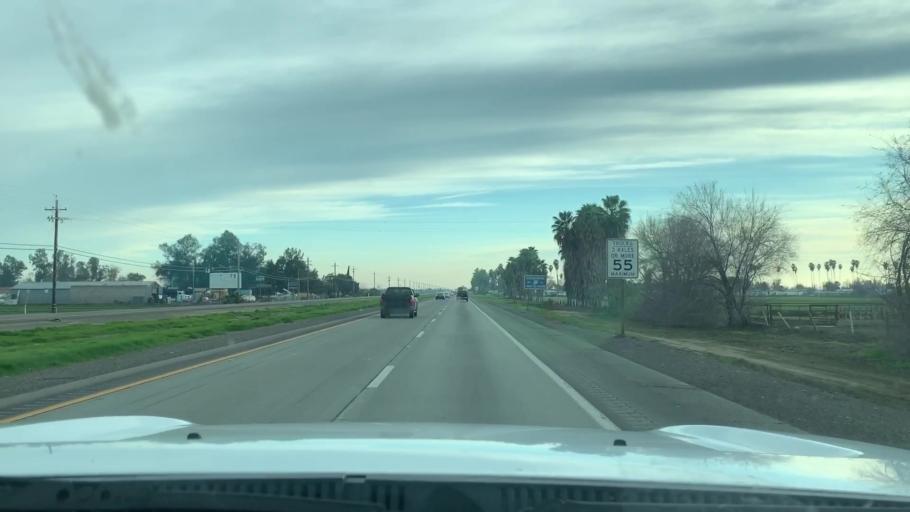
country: US
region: California
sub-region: Kings County
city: Lemoore
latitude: 36.3379
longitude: -119.8083
